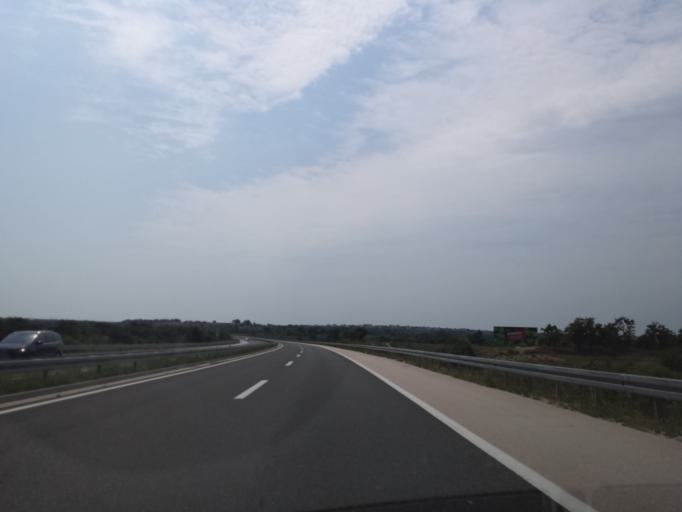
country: HR
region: Zadarska
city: Policnik
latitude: 44.1699
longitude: 15.4222
